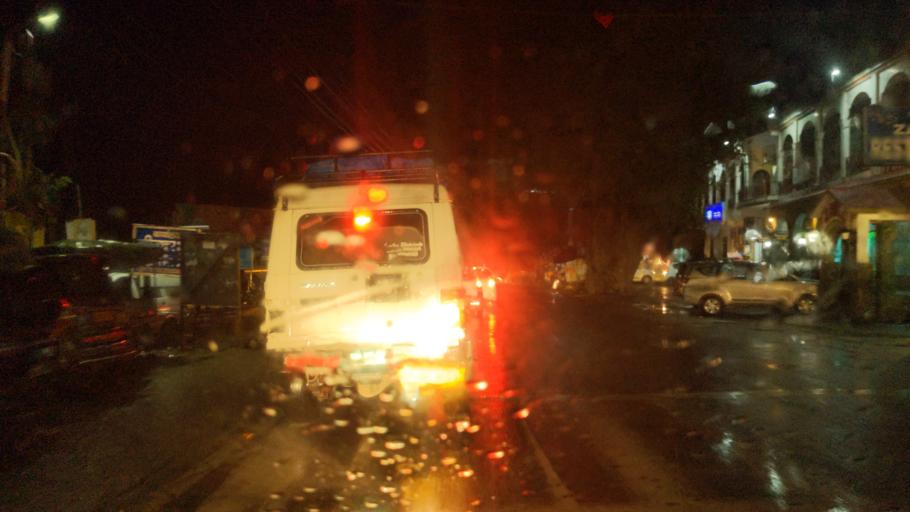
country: IN
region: Uttarakhand
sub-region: Naini Tal
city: Haldwani
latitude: 29.2698
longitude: 79.5441
